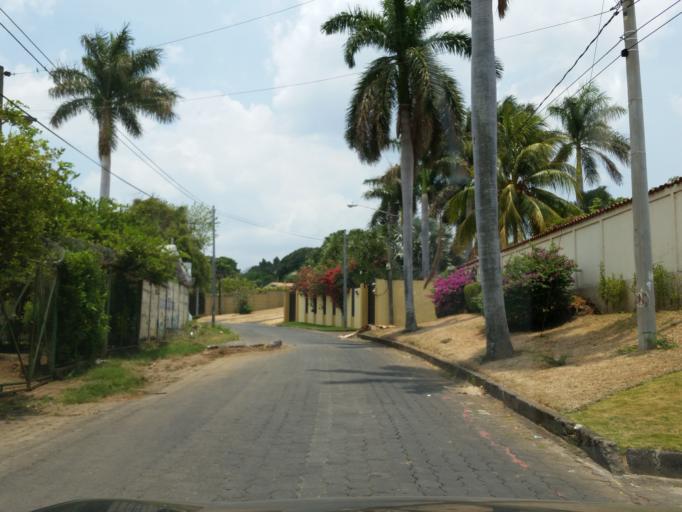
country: NI
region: Managua
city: Managua
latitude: 12.0984
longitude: -86.2358
